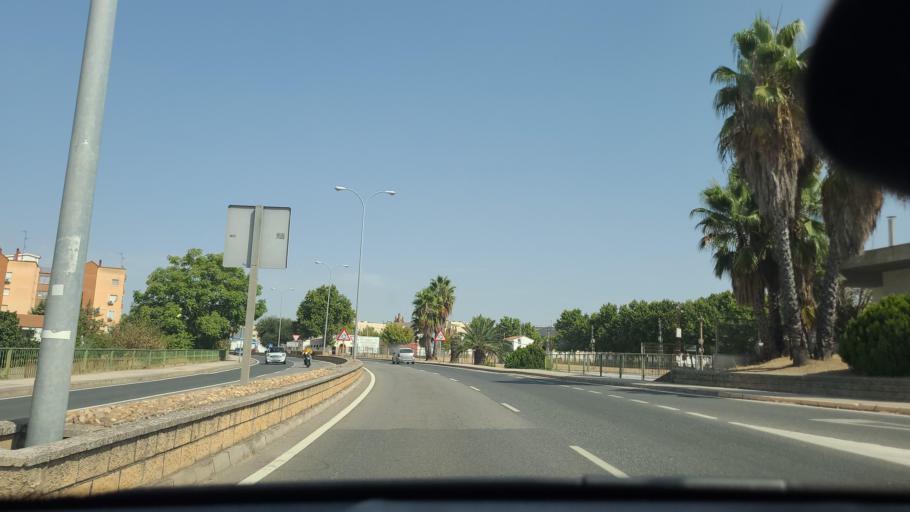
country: ES
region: Extremadura
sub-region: Provincia de Badajoz
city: Zafra
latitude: 38.4273
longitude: -6.4116
